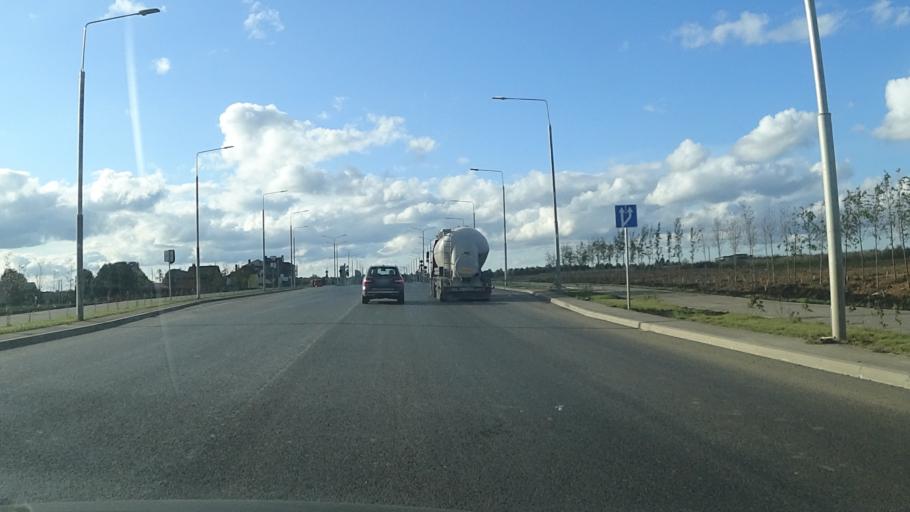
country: RU
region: Moskovskaya
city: Kommunarka
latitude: 55.5591
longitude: 37.4242
